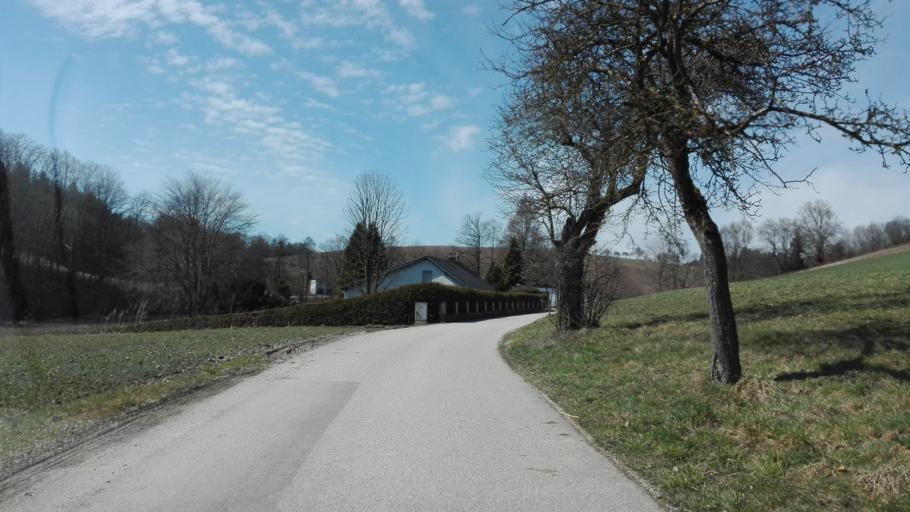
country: AT
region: Upper Austria
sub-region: Politischer Bezirk Grieskirchen
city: Bad Schallerbach
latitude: 48.2365
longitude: 13.8768
